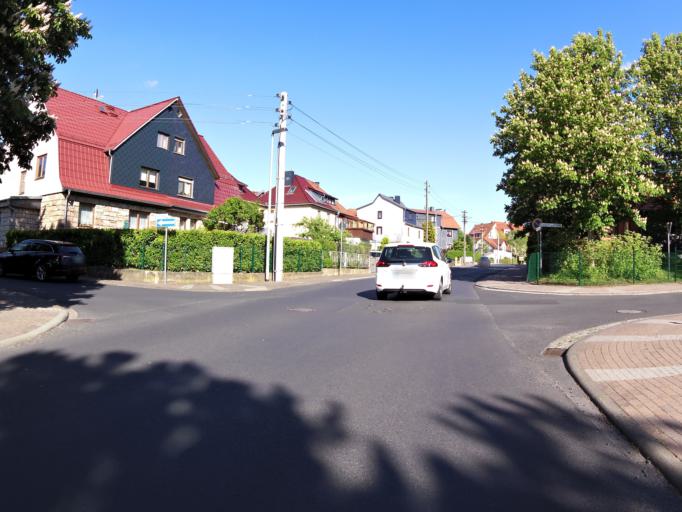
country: DE
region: Thuringia
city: Bad Salzungen
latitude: 50.8099
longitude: 10.2261
